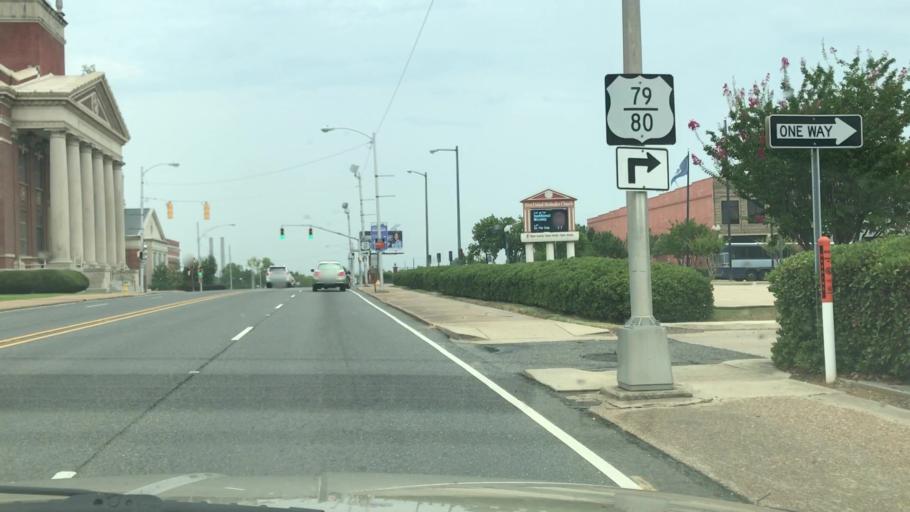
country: US
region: Louisiana
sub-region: Caddo Parish
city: Shreveport
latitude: 32.5103
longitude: -93.7521
